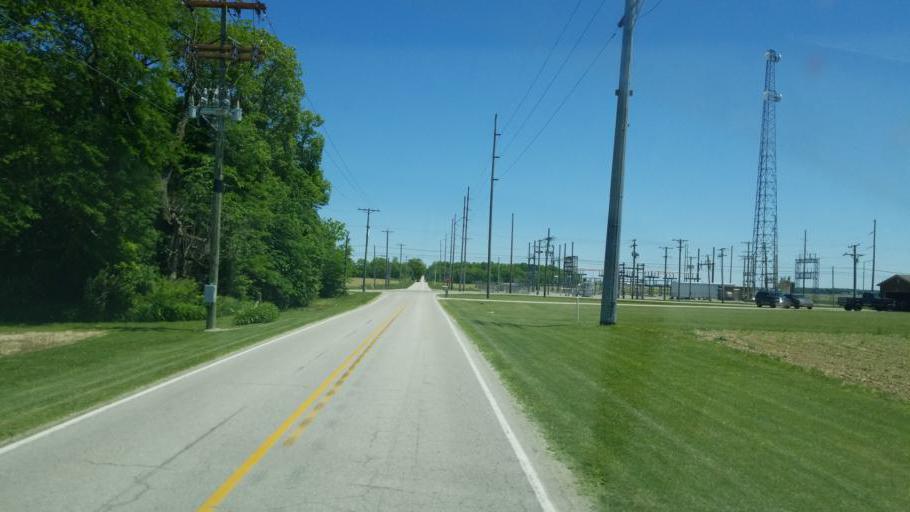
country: US
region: Ohio
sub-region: Darke County
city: Ansonia
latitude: 40.2648
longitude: -84.6378
